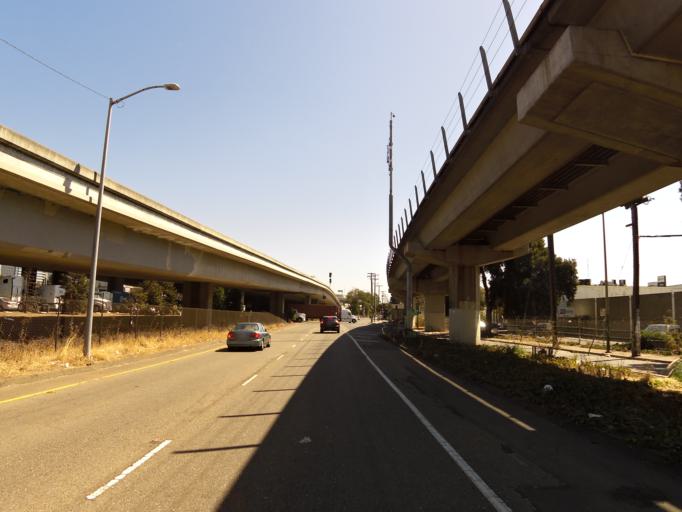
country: US
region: California
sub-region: Alameda County
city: Oakland
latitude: 37.8017
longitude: -122.2846
